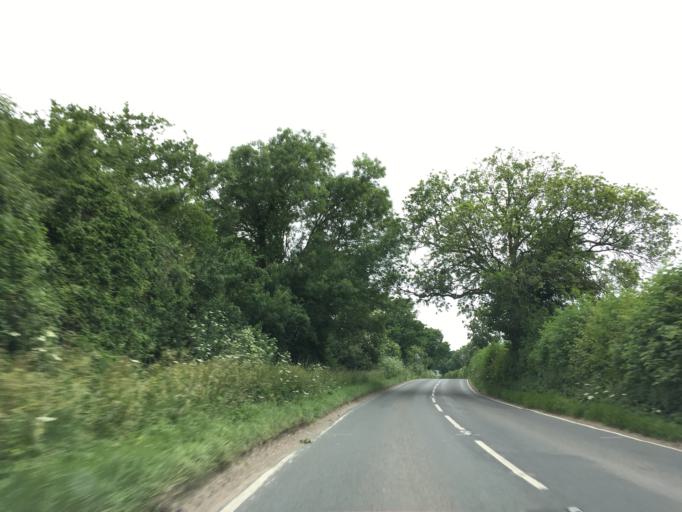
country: GB
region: England
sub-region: Gloucestershire
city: Stonehouse
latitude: 51.7622
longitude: -2.3454
